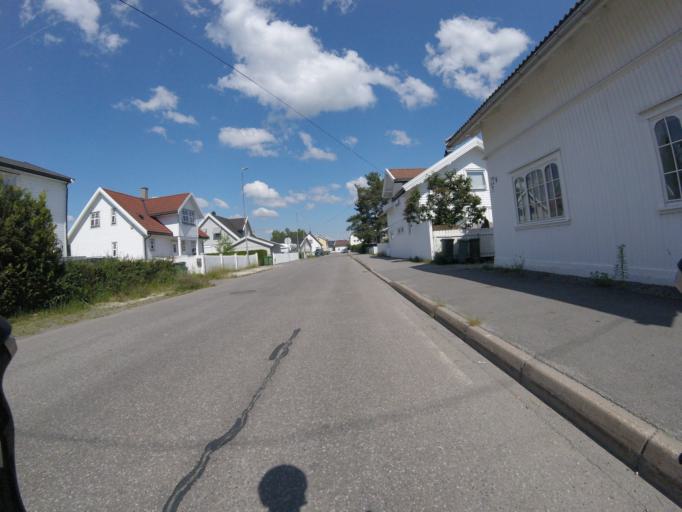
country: NO
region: Akershus
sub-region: Skedsmo
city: Lillestrom
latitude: 59.9502
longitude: 11.0608
